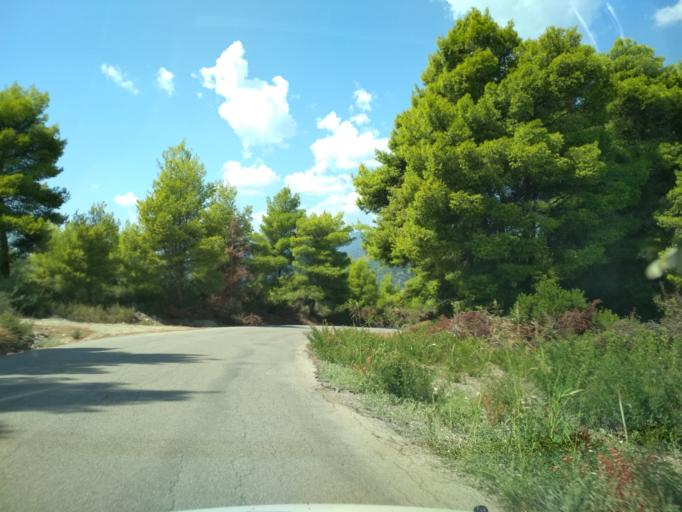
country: GR
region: Central Greece
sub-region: Nomos Evvoias
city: Roviai
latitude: 38.8211
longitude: 23.2328
